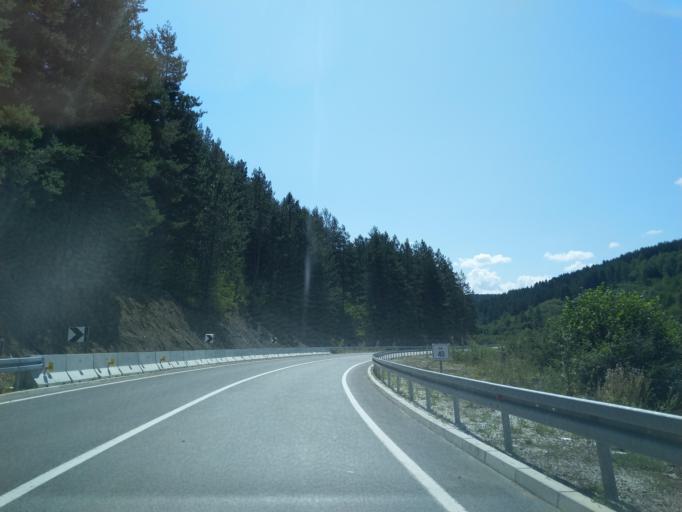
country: RS
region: Central Serbia
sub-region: Zlatiborski Okrug
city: Sjenica
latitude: 43.2855
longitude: 19.9462
